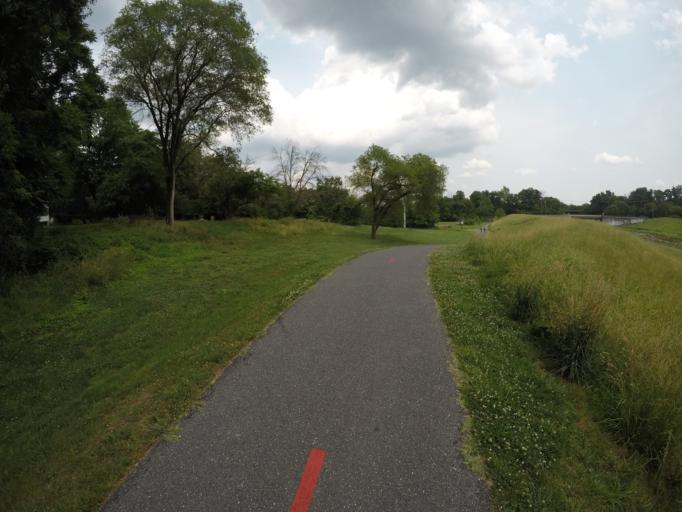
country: US
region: Maryland
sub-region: Prince George's County
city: Cottage City
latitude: 38.9469
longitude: -76.9487
